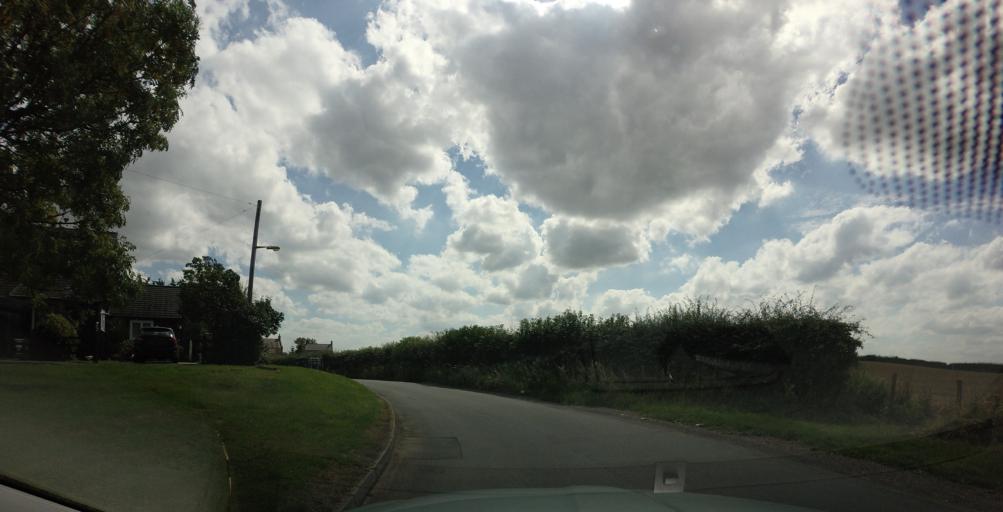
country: GB
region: England
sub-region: North Yorkshire
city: Ripon
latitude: 54.1302
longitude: -1.4856
